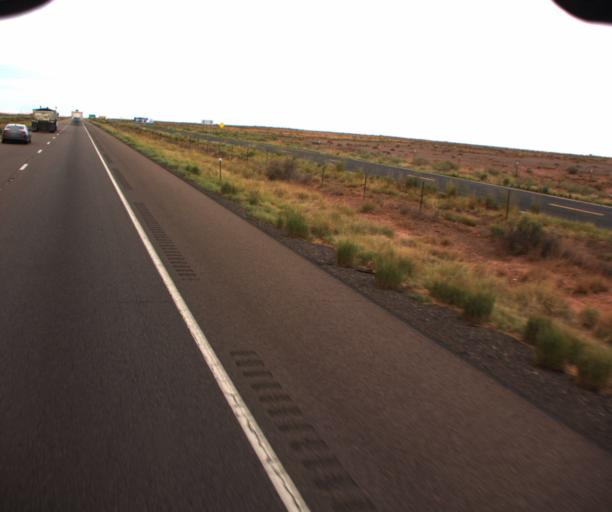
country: US
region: Arizona
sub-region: Coconino County
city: LeChee
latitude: 35.0724
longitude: -110.8516
